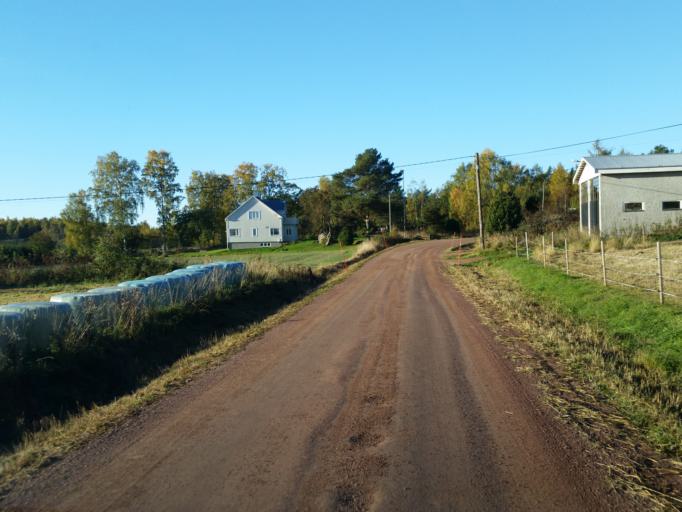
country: AX
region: Alands skaergard
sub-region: Vardoe
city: Vardoe
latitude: 60.2431
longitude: 20.3395
